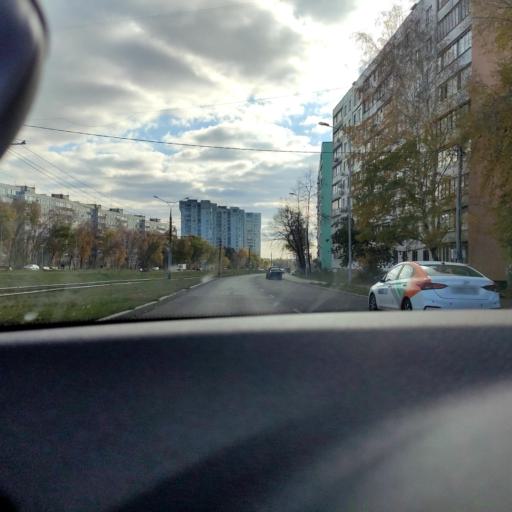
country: RU
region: Samara
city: Samara
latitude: 53.2548
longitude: 50.2462
